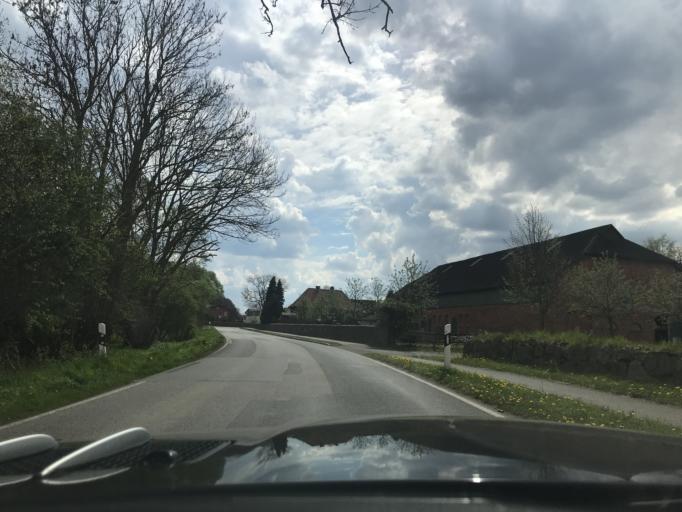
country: DE
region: Schleswig-Holstein
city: Timmendorfer Strand
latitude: 53.9506
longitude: 10.7903
